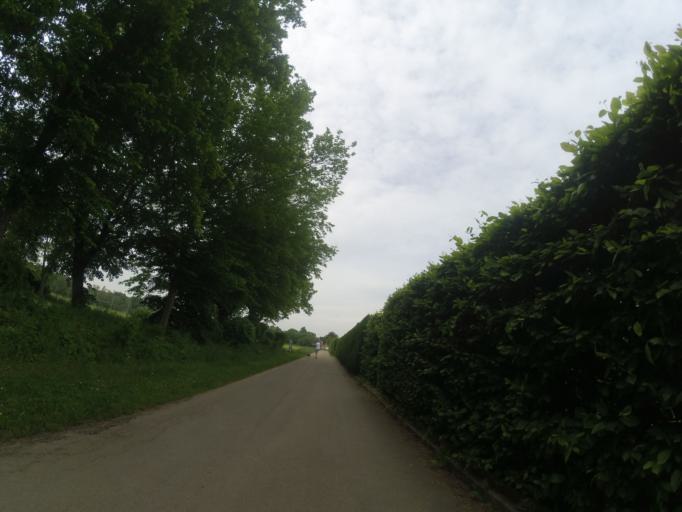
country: DE
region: Baden-Wuerttemberg
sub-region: Tuebingen Region
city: Huttisheim
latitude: 48.3271
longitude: 9.9361
